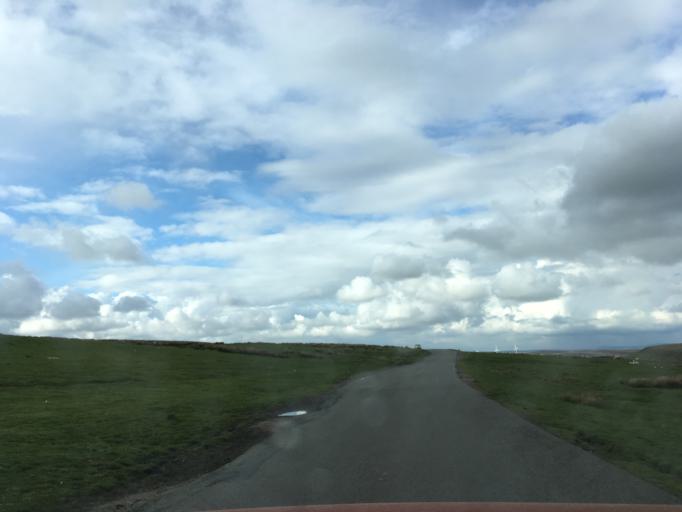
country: GB
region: Wales
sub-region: Caerphilly County Borough
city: Rhymney
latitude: 51.7252
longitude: -3.2976
